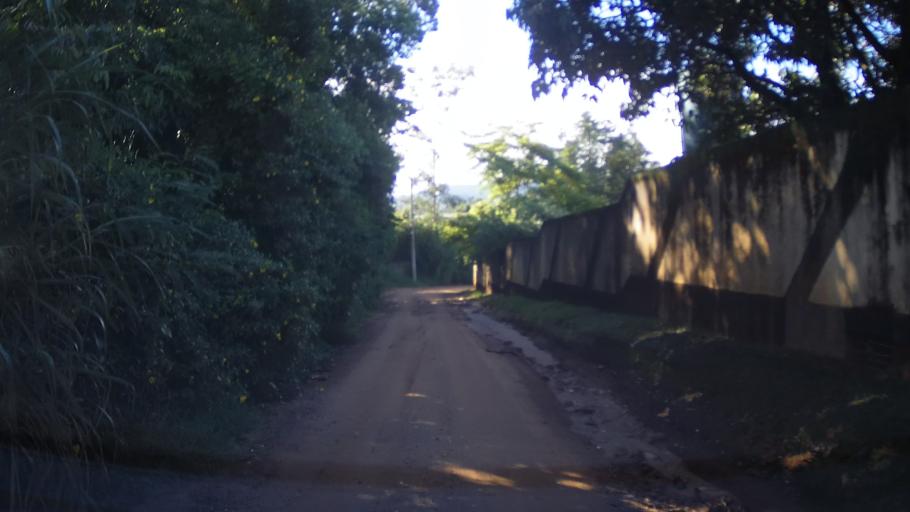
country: BR
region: Sao Paulo
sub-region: Itupeva
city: Itupeva
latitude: -23.1902
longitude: -46.9968
